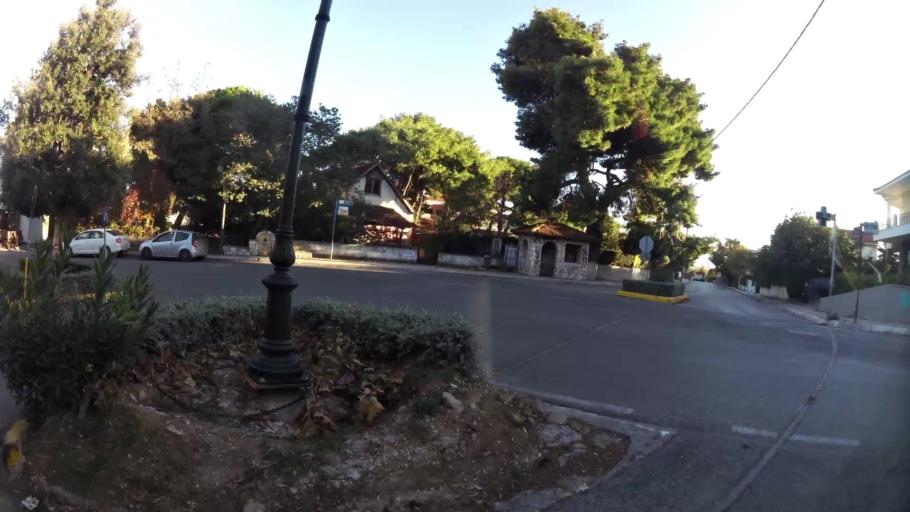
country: GR
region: Attica
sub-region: Nomarchia Anatolikis Attikis
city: Kryoneri
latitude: 38.1392
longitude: 23.8327
